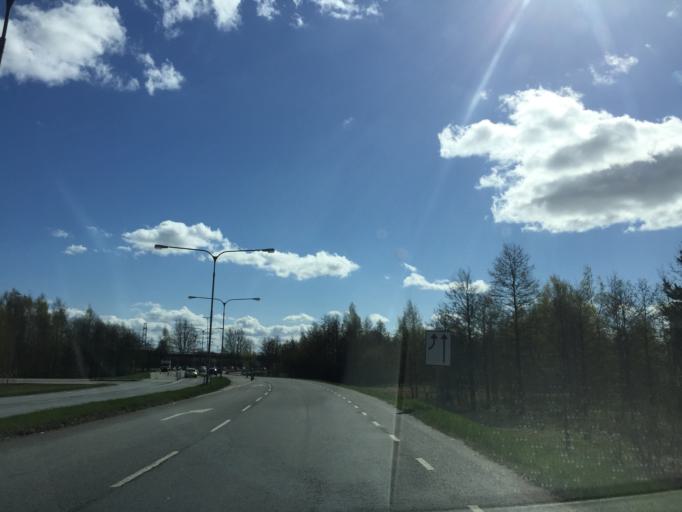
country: SE
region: OErebro
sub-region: Orebro Kommun
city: Orebro
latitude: 59.2693
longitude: 15.1734
